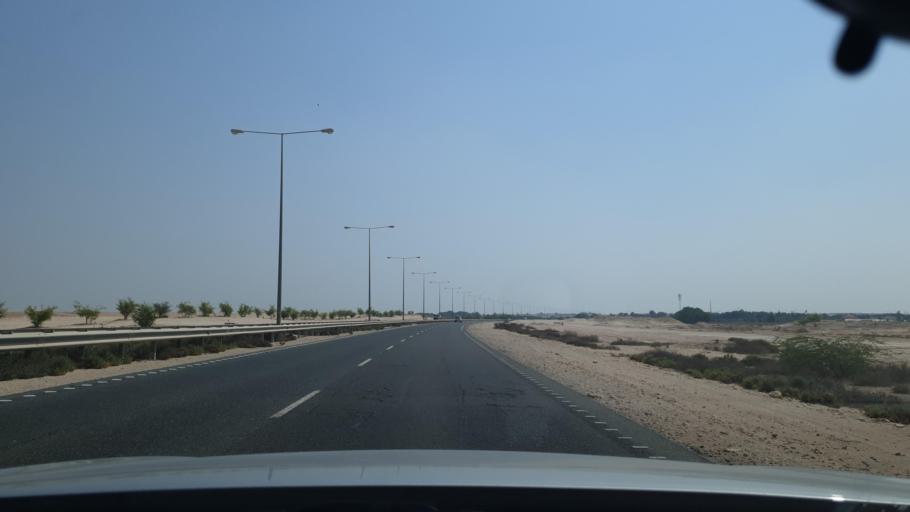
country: QA
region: Al Khawr
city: Al Khawr
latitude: 25.7369
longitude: 51.4906
